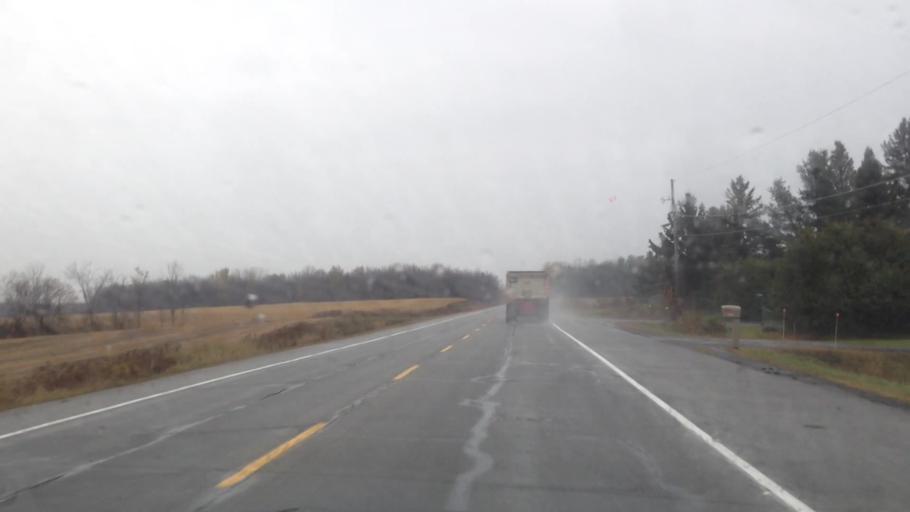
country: CA
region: Ontario
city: Clarence-Rockland
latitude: 45.3662
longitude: -75.3765
